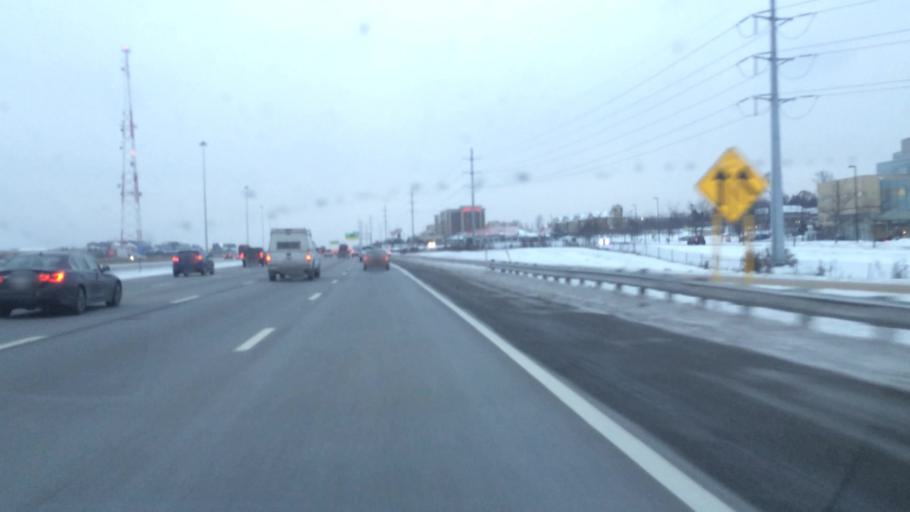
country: US
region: Ohio
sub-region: Cuyahoga County
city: Orange
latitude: 41.4523
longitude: -81.4907
